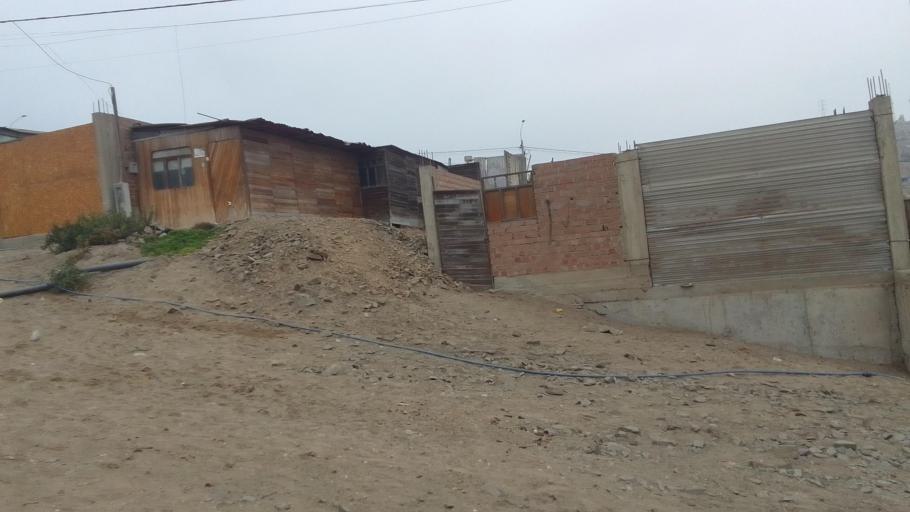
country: PE
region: Lima
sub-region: Lima
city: Santa Rosa
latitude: -11.8166
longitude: -77.1219
